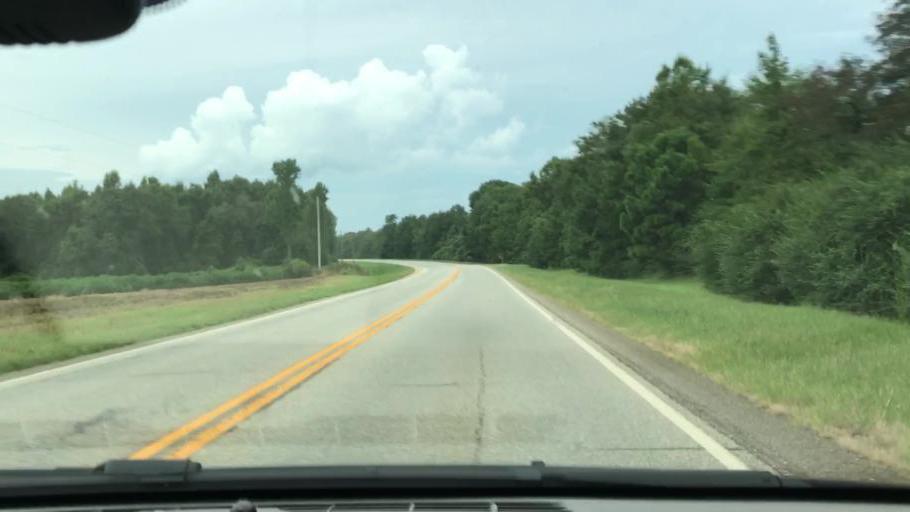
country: US
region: Georgia
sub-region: Early County
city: Blakely
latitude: 31.3143
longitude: -85.0409
